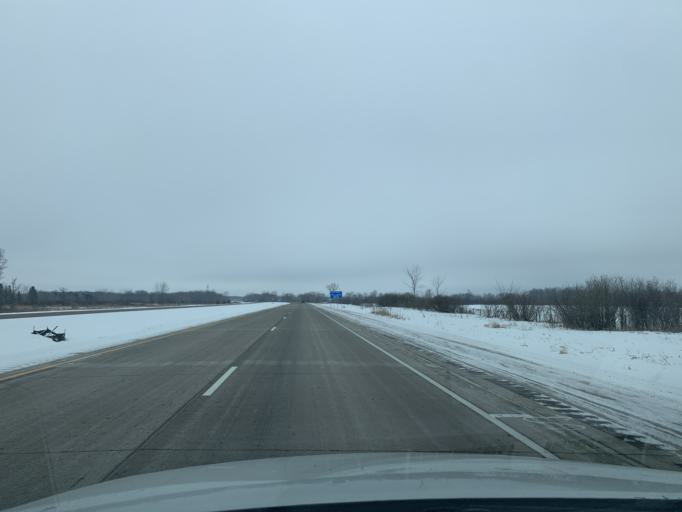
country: US
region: Minnesota
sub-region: Chisago County
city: Rush City
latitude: 45.6992
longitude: -92.9925
